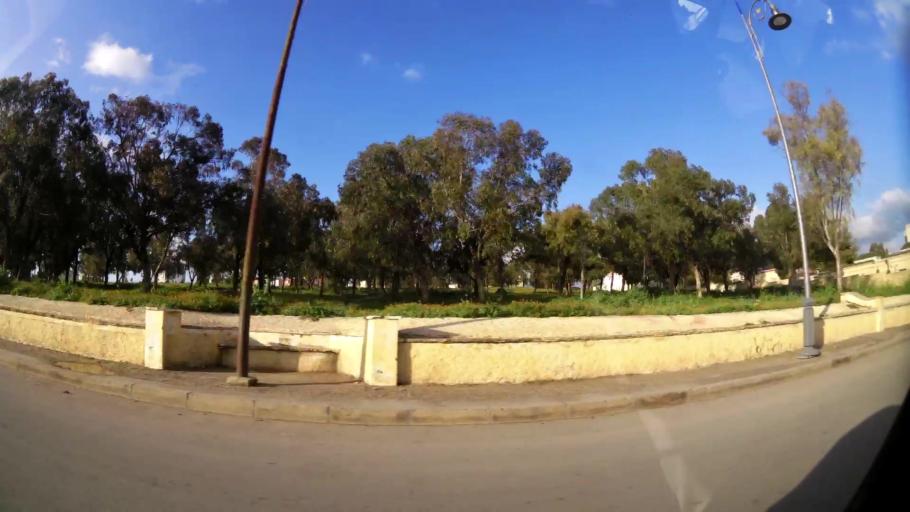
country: MA
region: Chaouia-Ouardigha
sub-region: Settat Province
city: Settat
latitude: 33.0045
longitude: -7.6148
